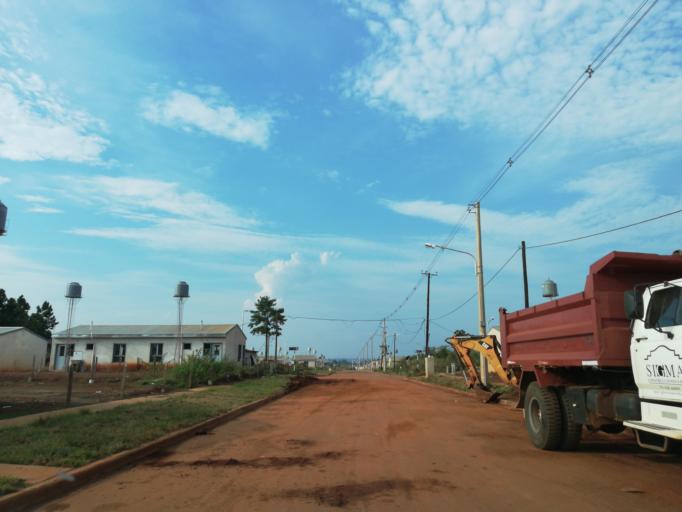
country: AR
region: Misiones
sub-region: Departamento de Capital
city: Posadas
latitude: -27.4024
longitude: -55.9912
